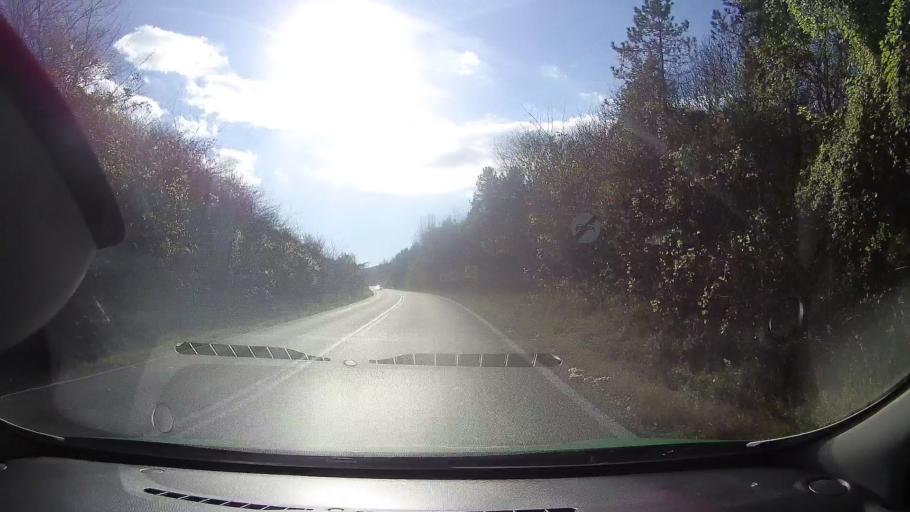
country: RO
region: Tulcea
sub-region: Oras Babadag
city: Babadag
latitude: 44.8705
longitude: 28.6884
